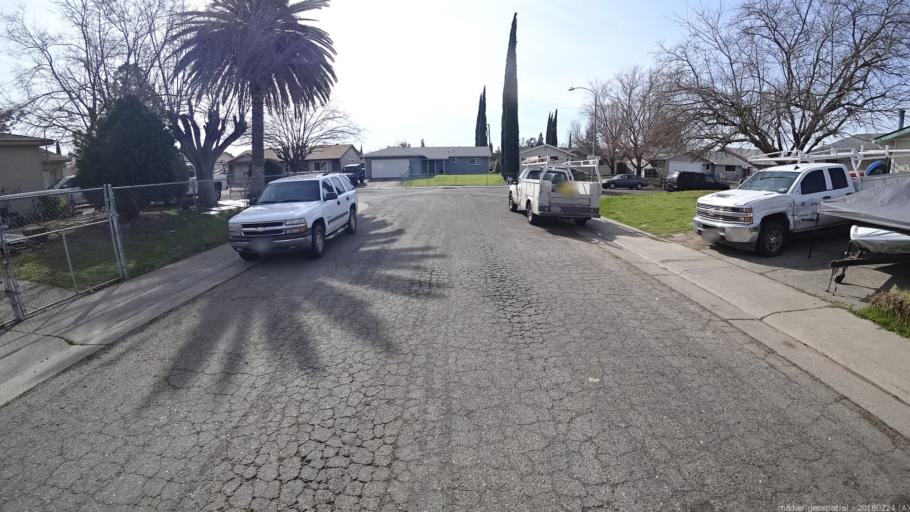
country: US
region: California
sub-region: Sacramento County
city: Rio Linda
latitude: 38.6775
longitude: -121.4417
